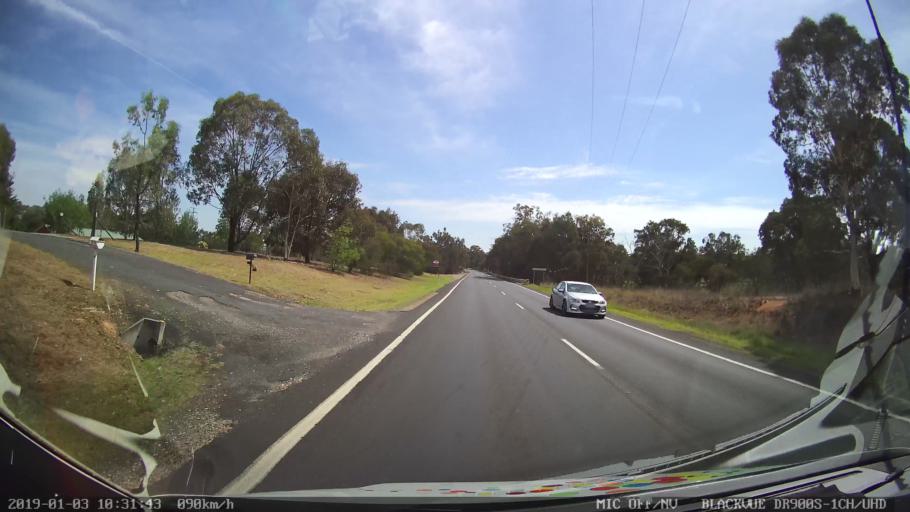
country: AU
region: New South Wales
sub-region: Young
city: Young
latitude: -34.3470
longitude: 148.2798
